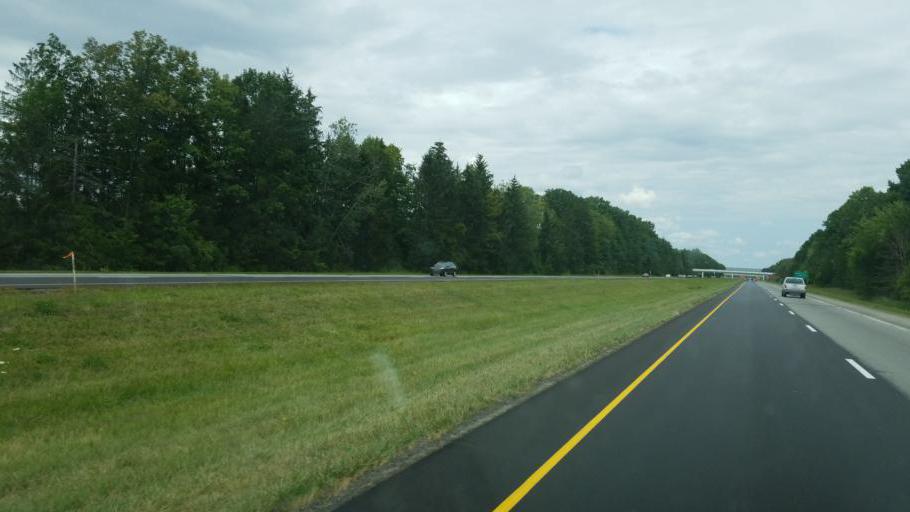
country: US
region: Ohio
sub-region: Mahoning County
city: Austintown
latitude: 41.0778
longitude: -80.7522
